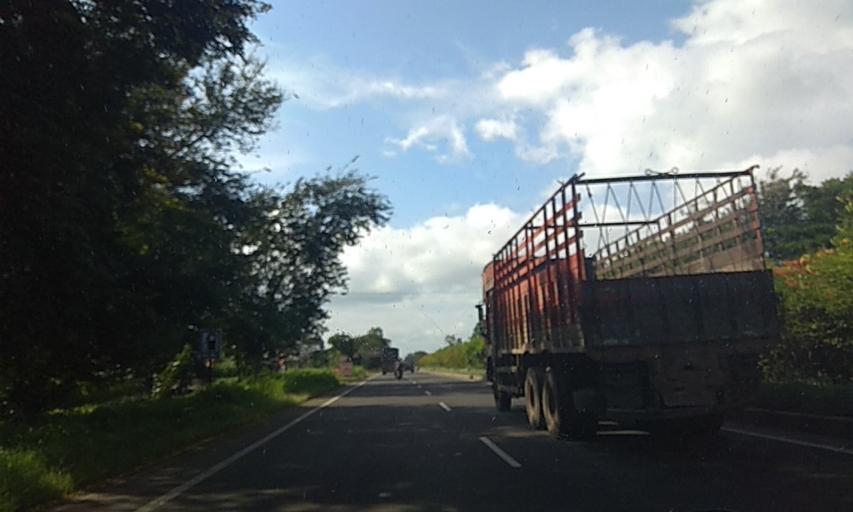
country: IN
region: Maharashtra
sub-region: Kolhapur
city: Kodoli
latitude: 17.0258
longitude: 74.2488
